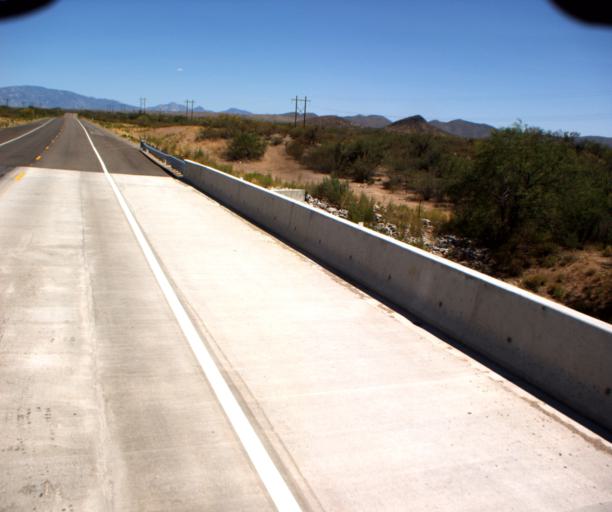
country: US
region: Arizona
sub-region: Pima County
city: Catalina
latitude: 32.6685
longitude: -111.0567
